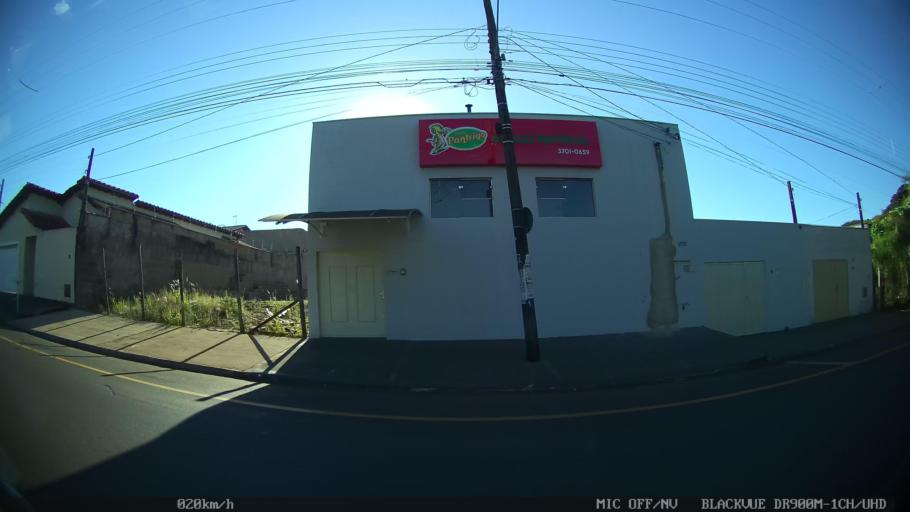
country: BR
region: Sao Paulo
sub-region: Franca
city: Franca
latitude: -20.5826
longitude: -47.3838
